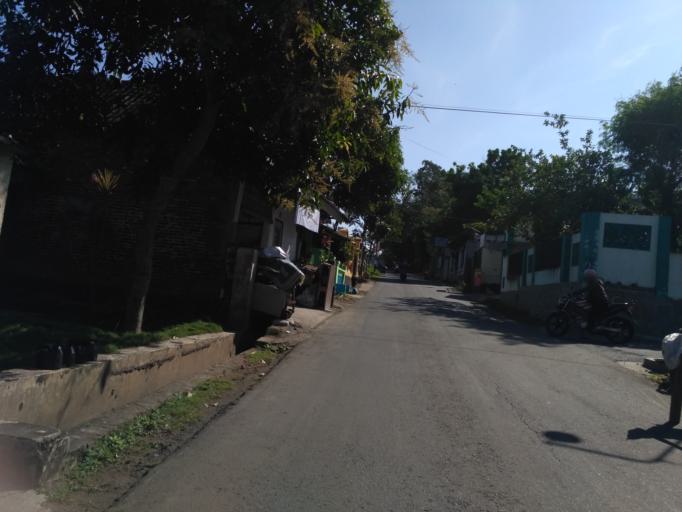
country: ID
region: East Java
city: Singosari
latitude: -7.9292
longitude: 112.6688
